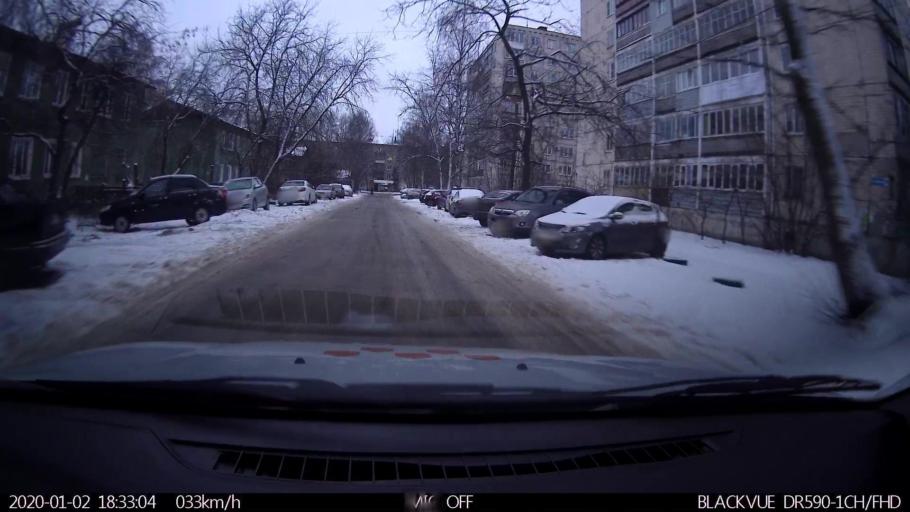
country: RU
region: Nizjnij Novgorod
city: Gorbatovka
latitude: 56.3326
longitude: 43.8368
